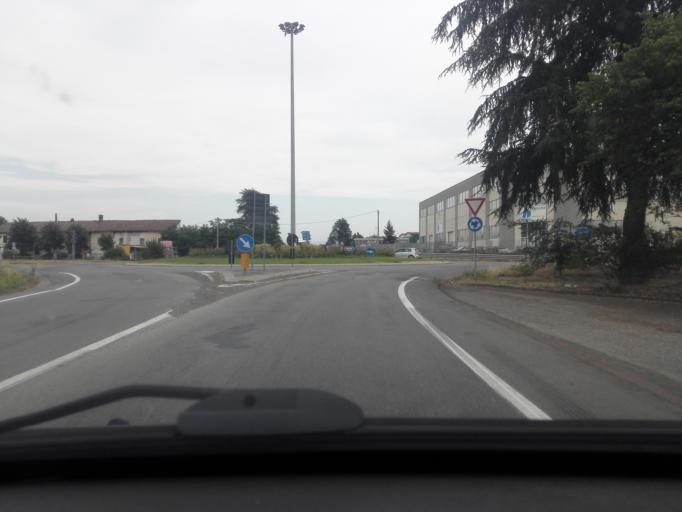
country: IT
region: Piedmont
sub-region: Provincia di Alessandria
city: Mandrogne
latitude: 44.8383
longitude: 8.7329
